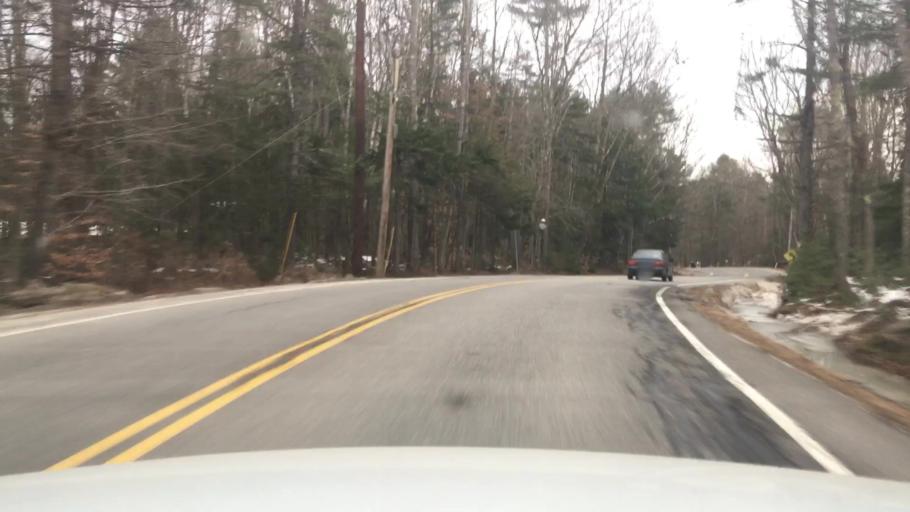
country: US
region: Maine
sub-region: Cumberland County
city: Freeport
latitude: 43.8786
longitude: -70.0450
